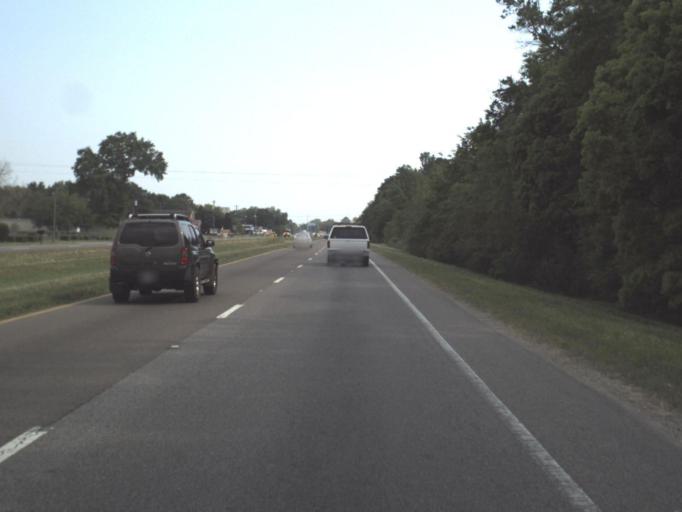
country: US
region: Florida
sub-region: Escambia County
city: Ensley
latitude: 30.5464
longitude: -87.2826
